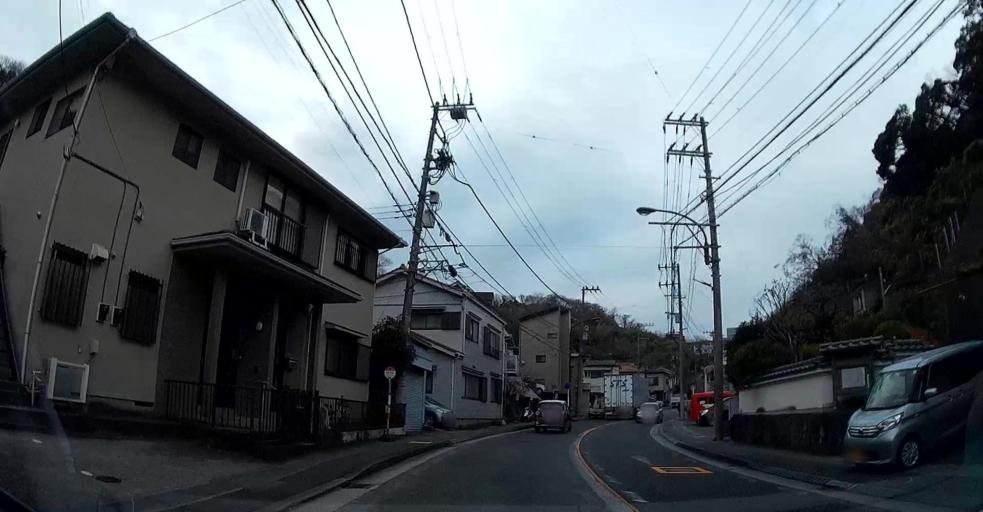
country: JP
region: Kanagawa
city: Yokosuka
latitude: 35.3064
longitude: 139.6369
